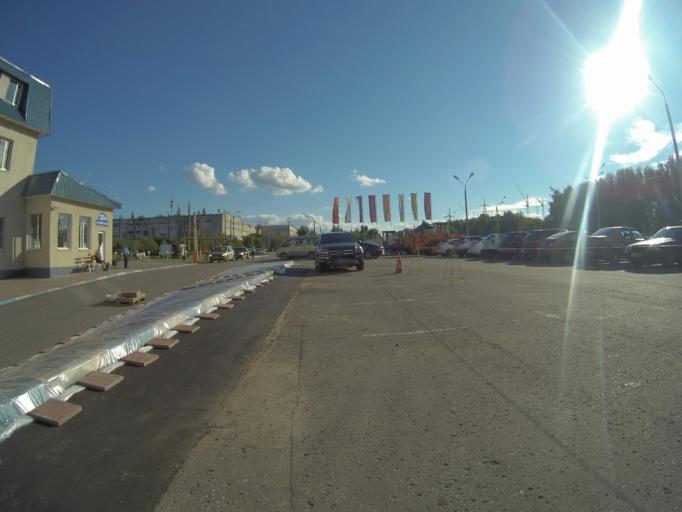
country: RU
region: Vladimir
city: Vladimir
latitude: 56.1658
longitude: 40.3868
